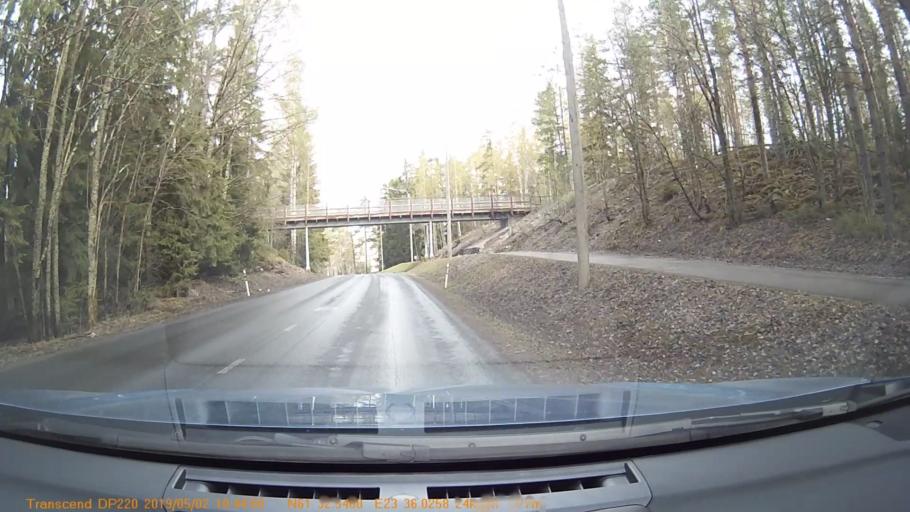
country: FI
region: Pirkanmaa
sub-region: Tampere
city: Yloejaervi
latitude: 61.5425
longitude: 23.6004
